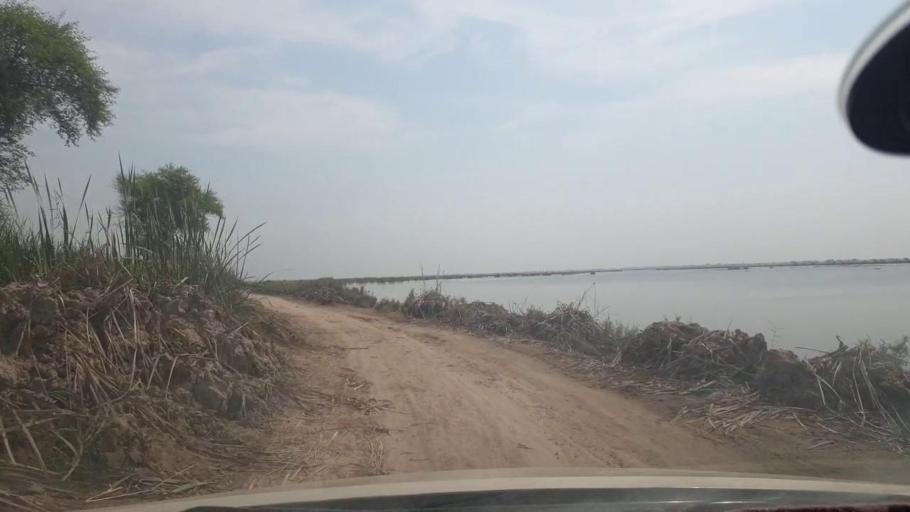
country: PK
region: Sindh
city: Jacobabad
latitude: 28.3104
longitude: 68.4798
